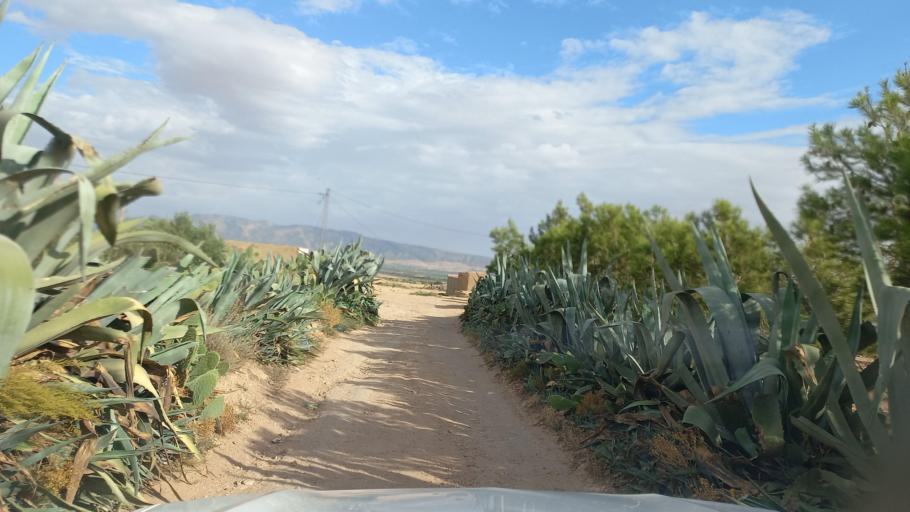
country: TN
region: Al Qasrayn
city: Sbiba
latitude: 35.4492
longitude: 9.0853
